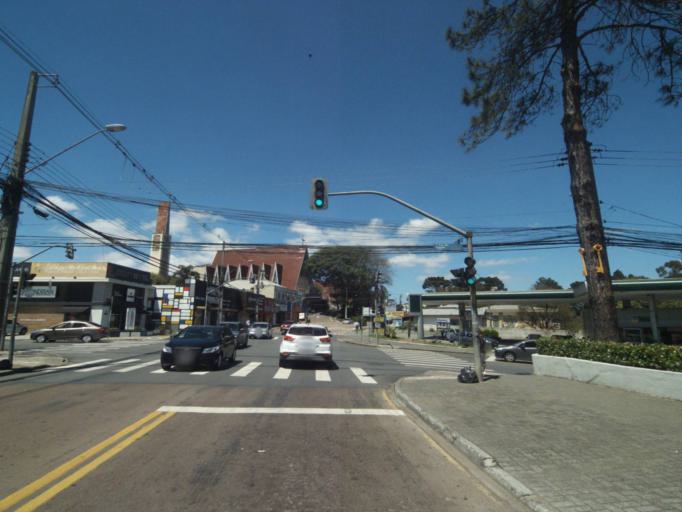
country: BR
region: Parana
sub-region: Curitiba
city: Curitiba
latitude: -25.3901
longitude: -49.2606
